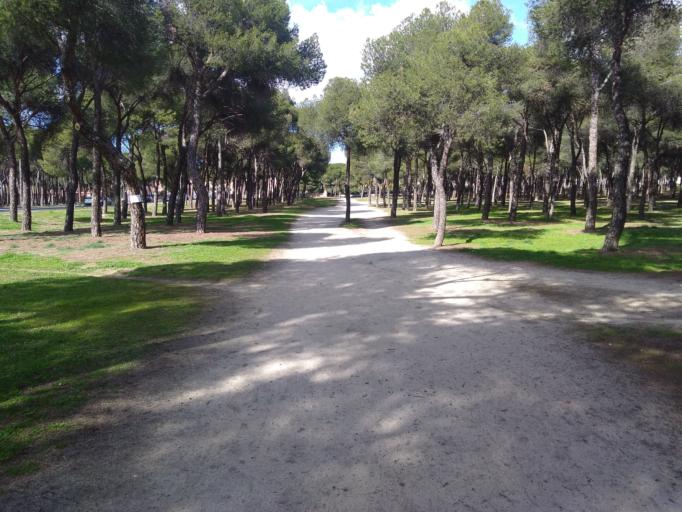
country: ES
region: Madrid
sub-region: Provincia de Madrid
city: Leganes
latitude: 40.3611
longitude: -3.7709
